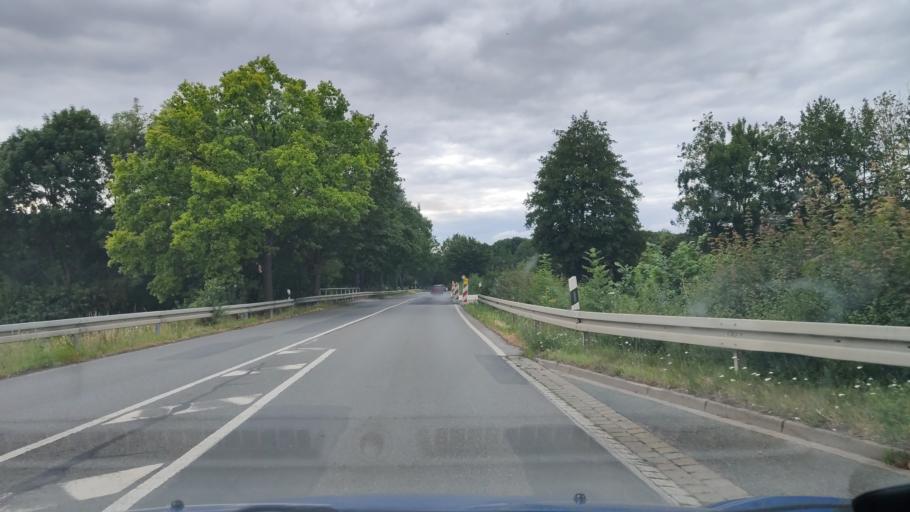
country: DE
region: Lower Saxony
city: Ronnenberg
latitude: 52.3100
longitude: 9.6791
